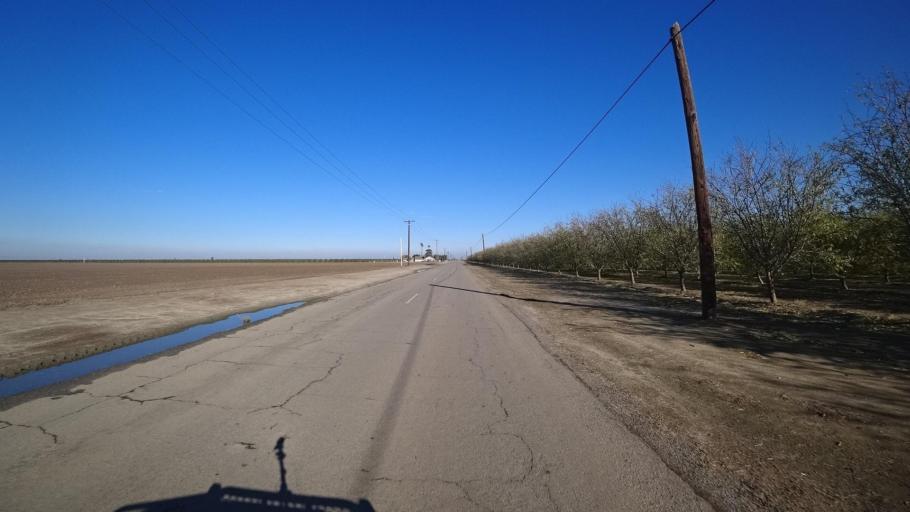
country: US
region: California
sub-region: Kern County
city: McFarland
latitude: 35.7074
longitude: -119.2764
